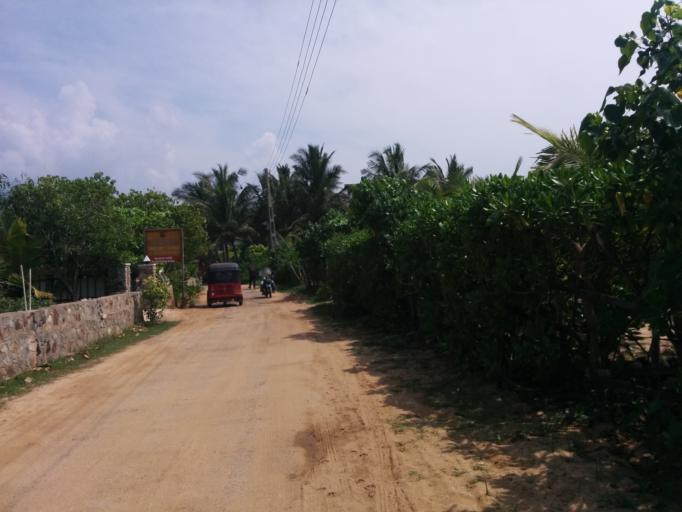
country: LK
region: Southern
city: Tangalla
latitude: 6.0371
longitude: 80.8059
